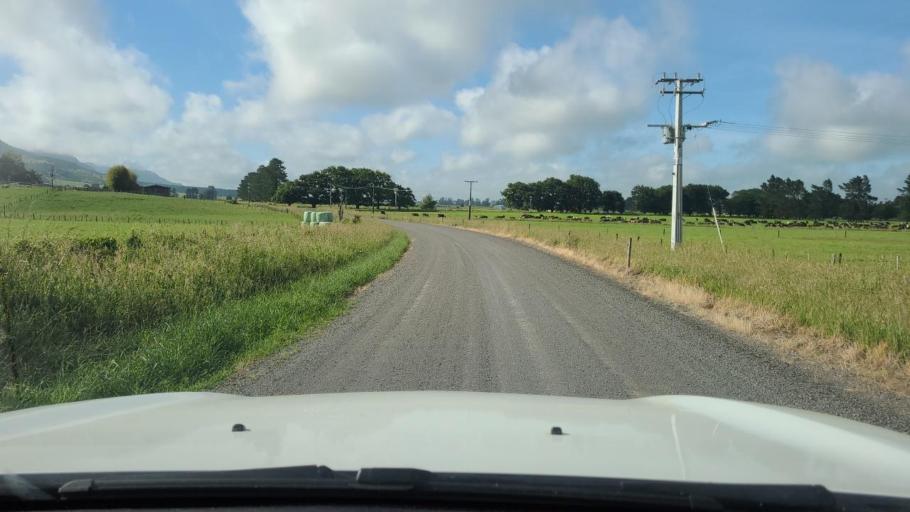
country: NZ
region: Bay of Plenty
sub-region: Western Bay of Plenty District
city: Katikati
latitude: -37.6135
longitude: 175.7955
